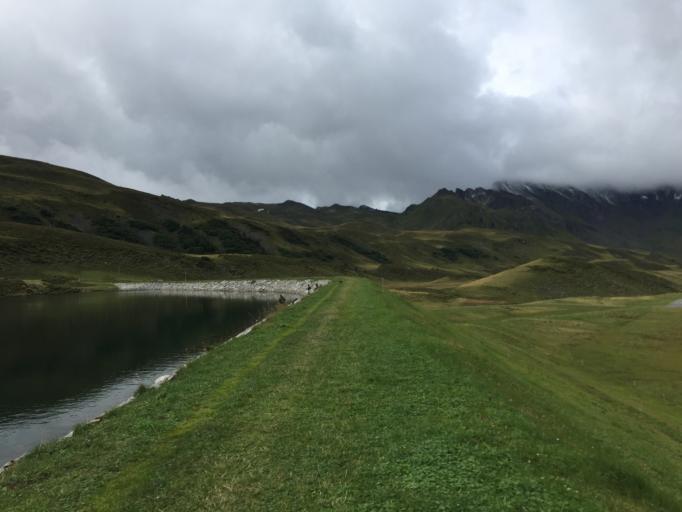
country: CH
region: Obwalden
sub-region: Obwalden
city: Engelberg
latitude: 46.7728
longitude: 8.3009
